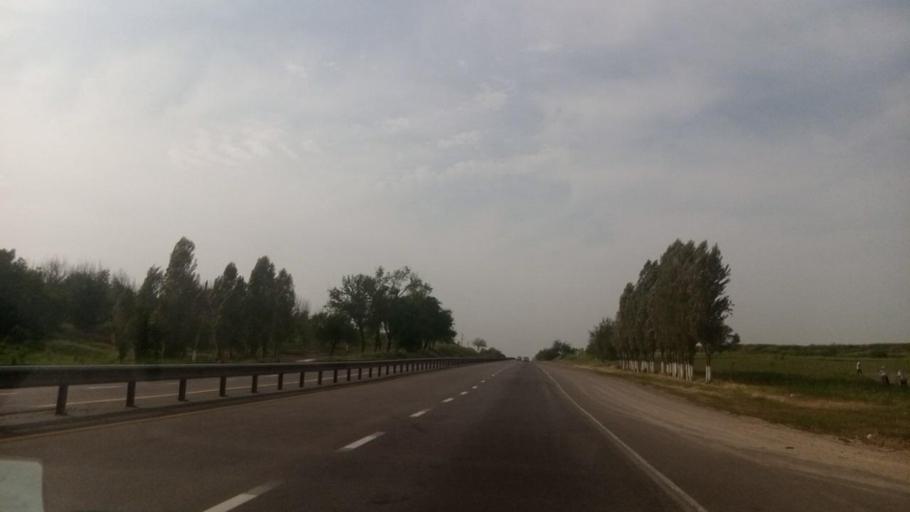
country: UZ
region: Toshkent
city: Tuytepa
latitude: 41.0796
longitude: 69.4709
